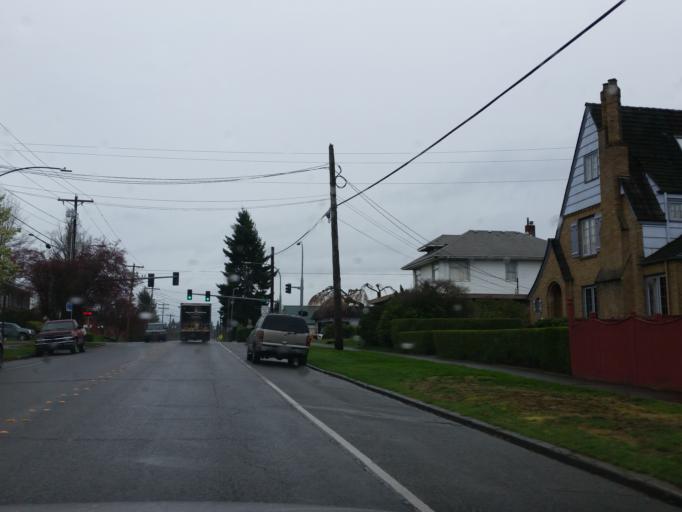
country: US
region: Washington
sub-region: Snohomish County
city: Snohomish
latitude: 47.9168
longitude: -122.0983
